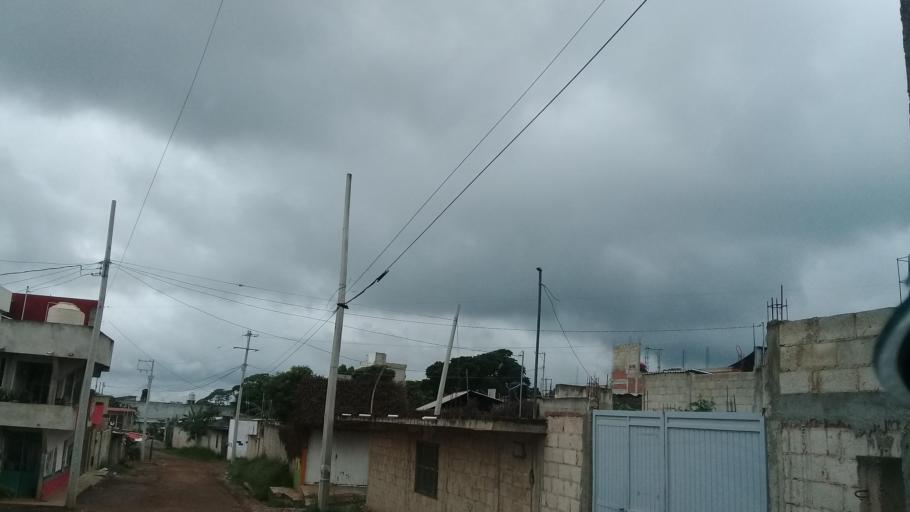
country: MX
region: Veracruz
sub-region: Emiliano Zapata
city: Las Trancas
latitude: 19.4968
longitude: -96.8625
